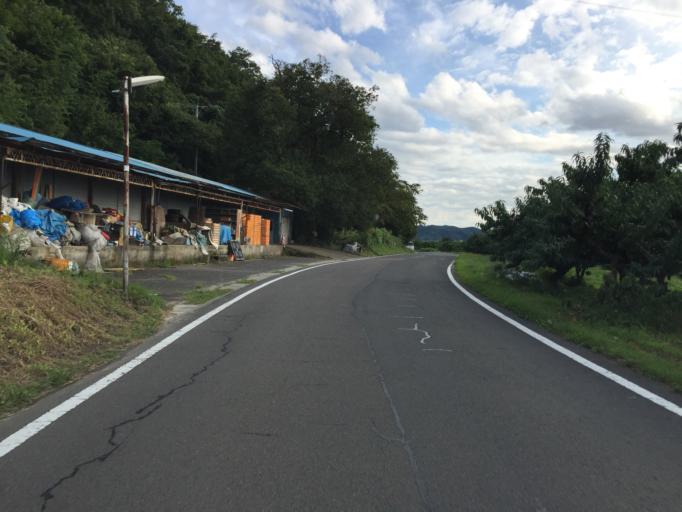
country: JP
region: Fukushima
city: Hobaramachi
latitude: 37.8032
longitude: 140.5096
